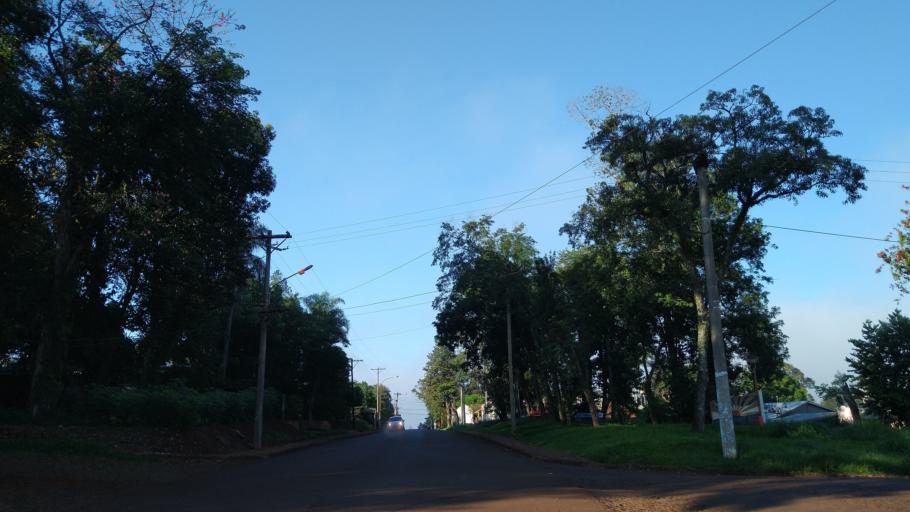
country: AR
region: Misiones
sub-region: Departamento de Montecarlo
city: Montecarlo
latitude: -26.5659
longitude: -54.7728
